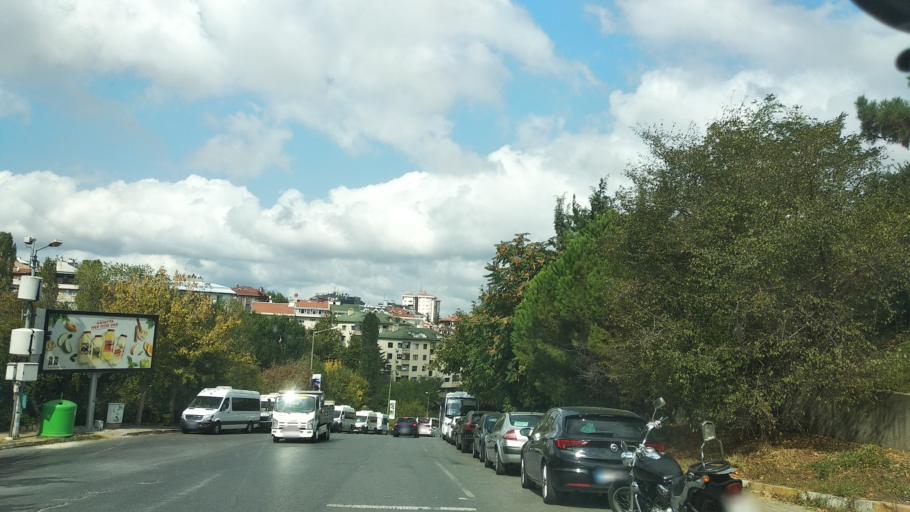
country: TR
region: Istanbul
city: Sisli
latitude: 41.0860
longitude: 29.0373
